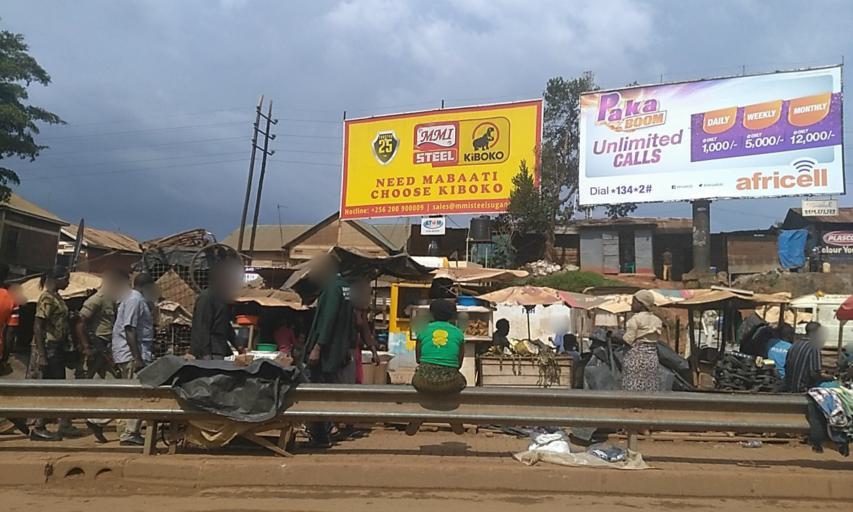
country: UG
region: Central Region
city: Kampala Central Division
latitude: 0.3070
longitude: 32.5167
